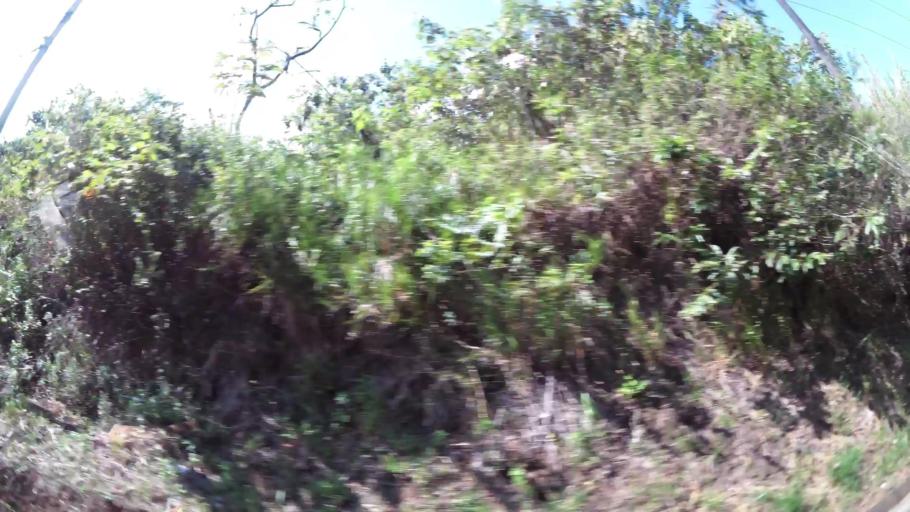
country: CO
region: Valle del Cauca
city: Cali
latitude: 3.4343
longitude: -76.5599
